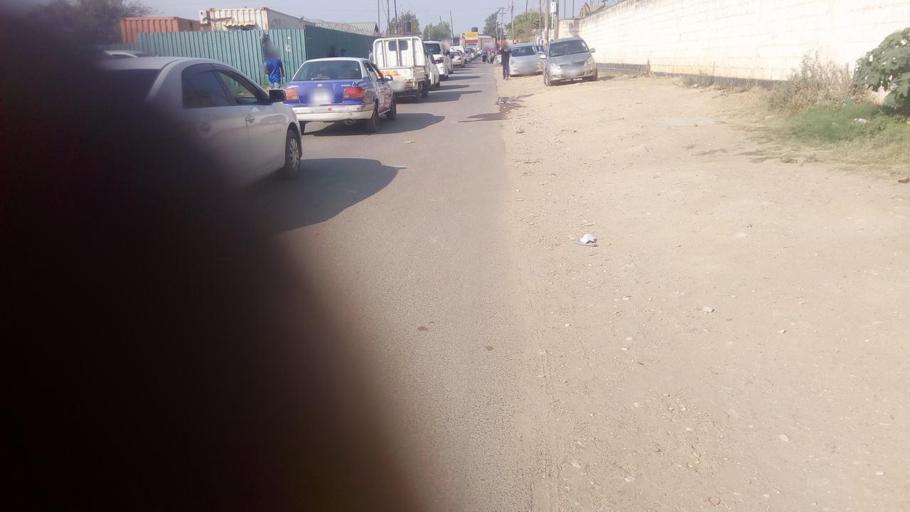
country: ZM
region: Lusaka
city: Lusaka
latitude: -15.3702
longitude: 28.2950
